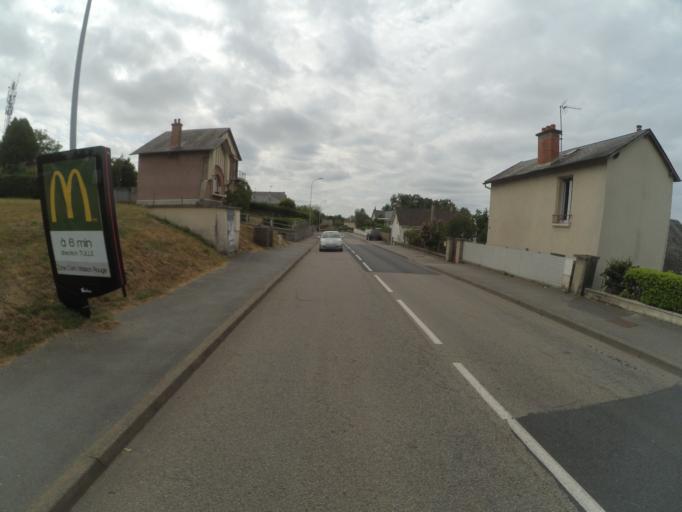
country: FR
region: Limousin
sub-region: Departement de la Correze
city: Ussel
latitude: 45.5529
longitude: 2.3032
